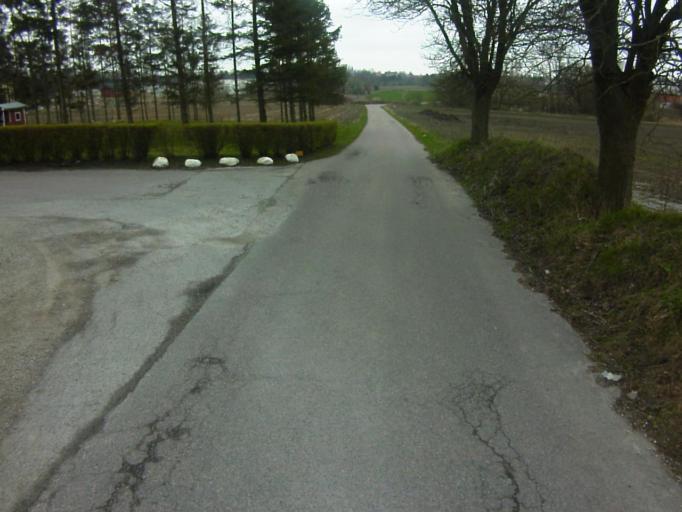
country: SE
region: Skane
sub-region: Kavlinge Kommun
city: Kaevlinge
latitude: 55.7880
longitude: 13.0994
